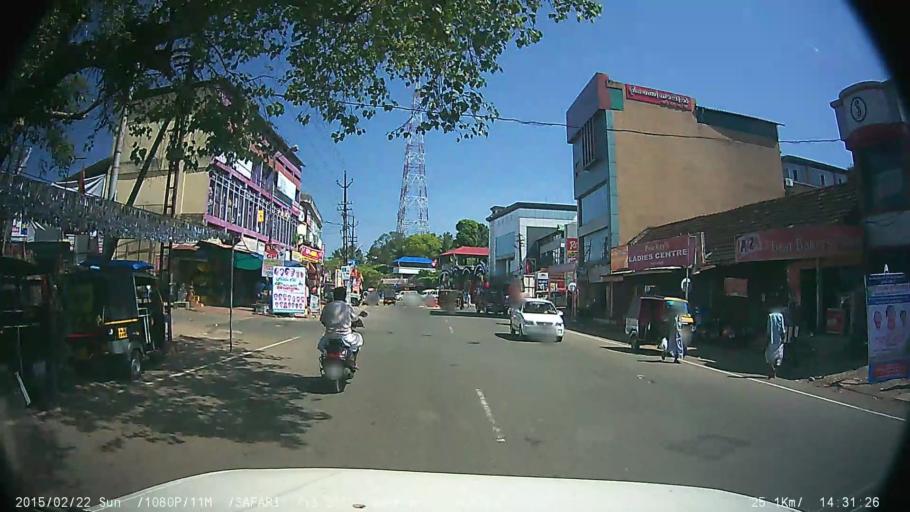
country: IN
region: Kerala
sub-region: Kottayam
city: Erattupetta
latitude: 9.5653
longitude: 76.7551
